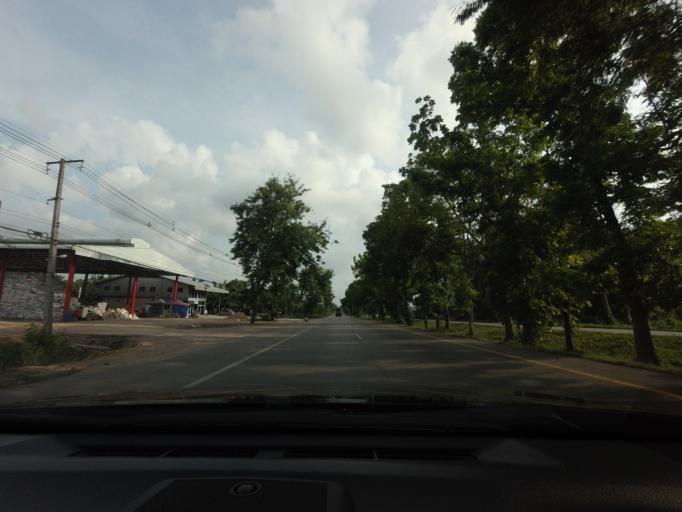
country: TH
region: Chumphon
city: Sawi
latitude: 10.2052
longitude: 99.0983
